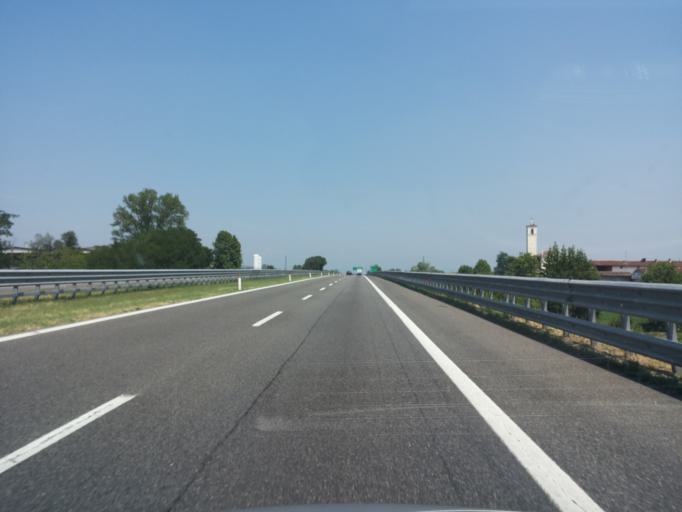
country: IT
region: Lombardy
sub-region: Provincia di Brescia
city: Alfianello
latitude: 45.2609
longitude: 10.1258
